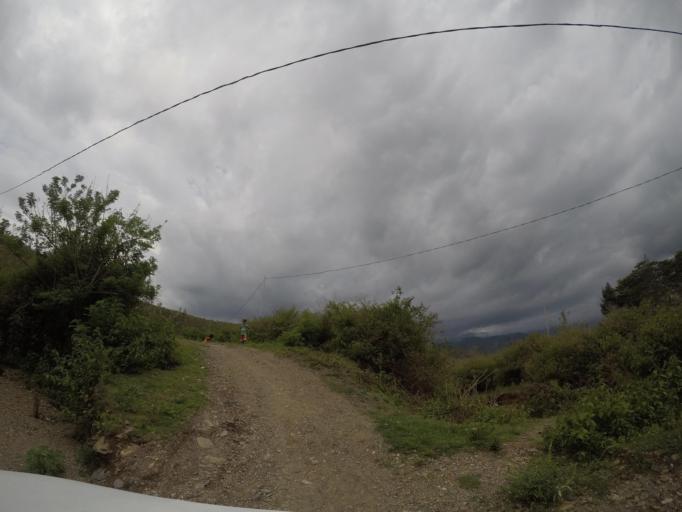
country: TL
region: Ermera
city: Gleno
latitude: -8.7060
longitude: 125.4505
